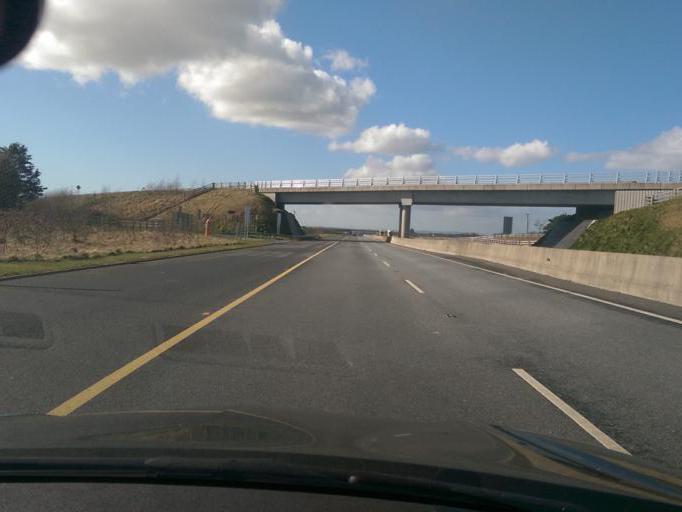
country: IE
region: Connaught
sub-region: County Galway
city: Athenry
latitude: 53.2979
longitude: -8.8248
